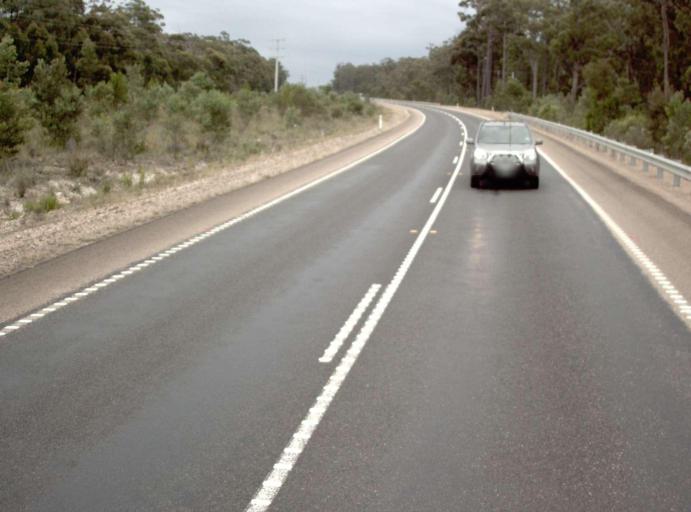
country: AU
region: Victoria
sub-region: East Gippsland
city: Lakes Entrance
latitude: -37.6974
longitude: 148.0485
